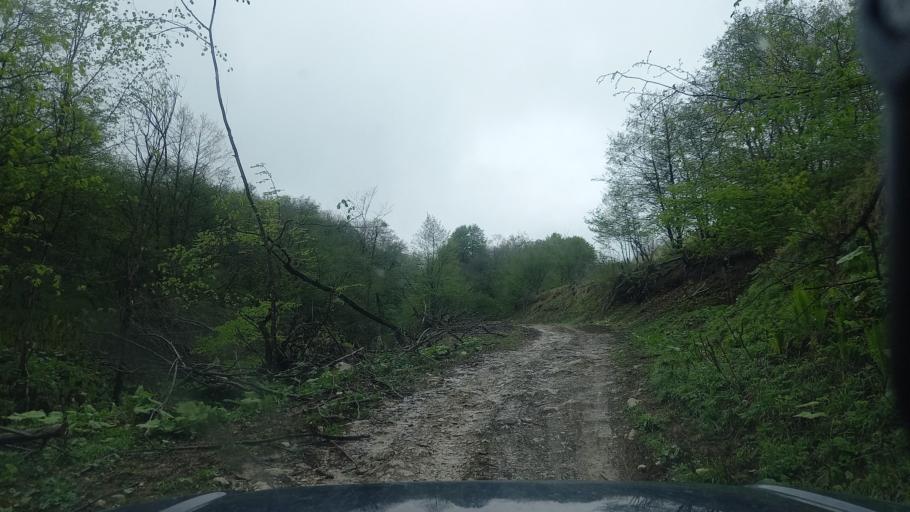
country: RU
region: Kabardino-Balkariya
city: Babugent
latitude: 43.2124
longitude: 43.5463
